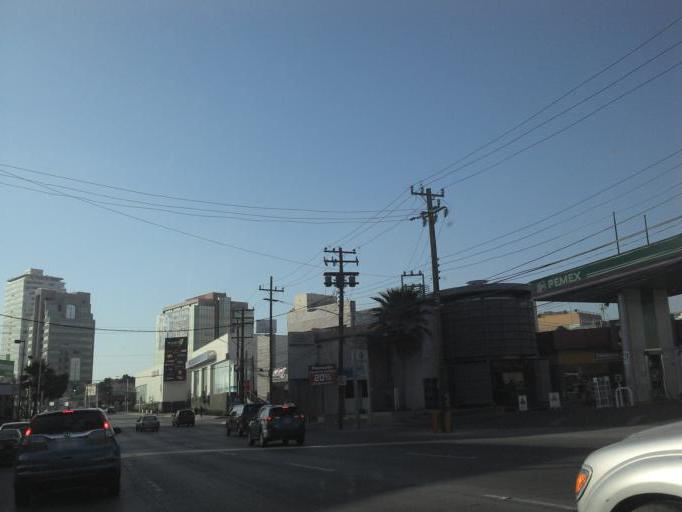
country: MX
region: Baja California
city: Tijuana
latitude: 32.5160
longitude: -117.0125
